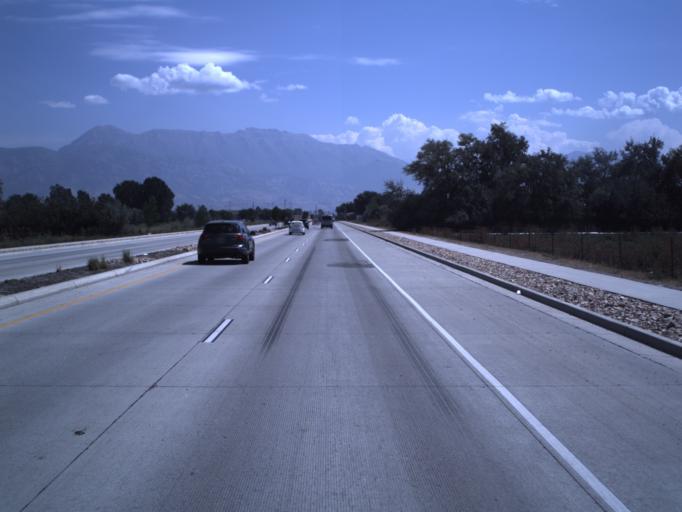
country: US
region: Utah
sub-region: Utah County
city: Saratoga Springs
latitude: 40.3761
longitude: -111.8937
